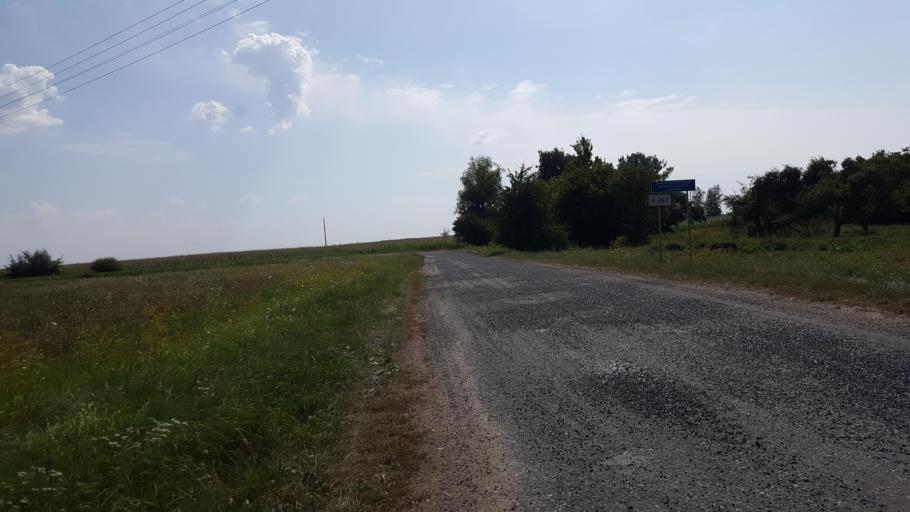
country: PL
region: Podlasie
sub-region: Powiat hajnowski
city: Czeremcha
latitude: 52.4964
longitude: 23.5640
